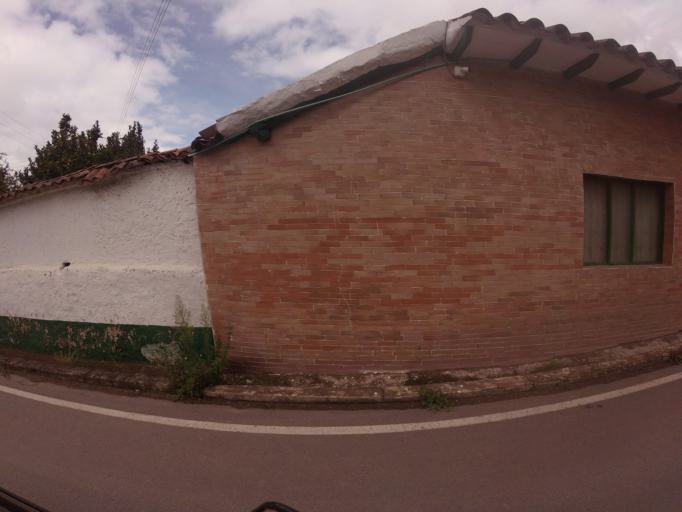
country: CO
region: Boyaca
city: Nobsa
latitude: 5.7904
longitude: -72.9737
